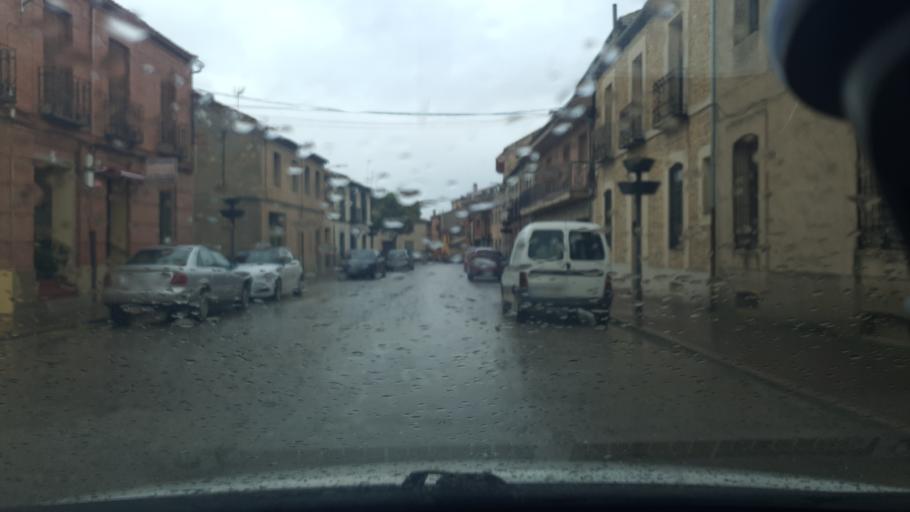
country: ES
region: Castille and Leon
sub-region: Provincia de Segovia
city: Carbonero el Mayor
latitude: 41.1204
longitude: -4.2648
